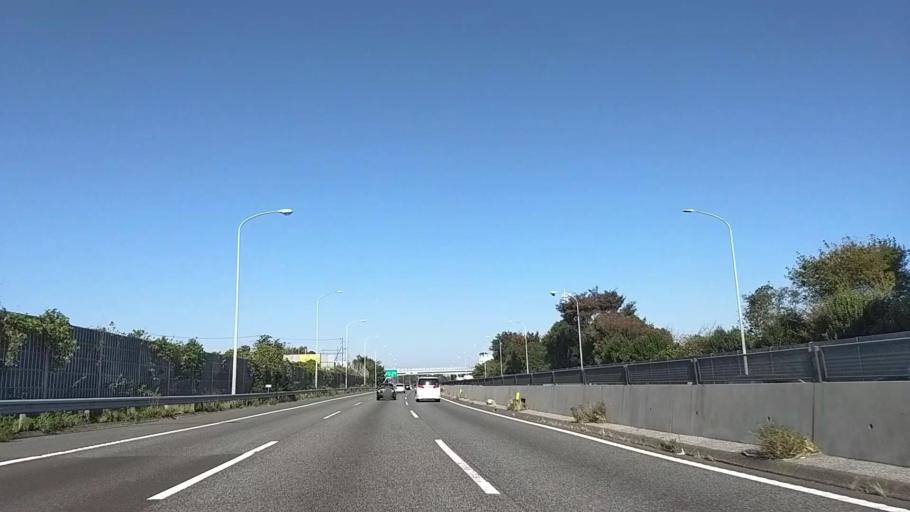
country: JP
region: Kanagawa
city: Yokohama
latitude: 35.4581
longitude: 139.5469
